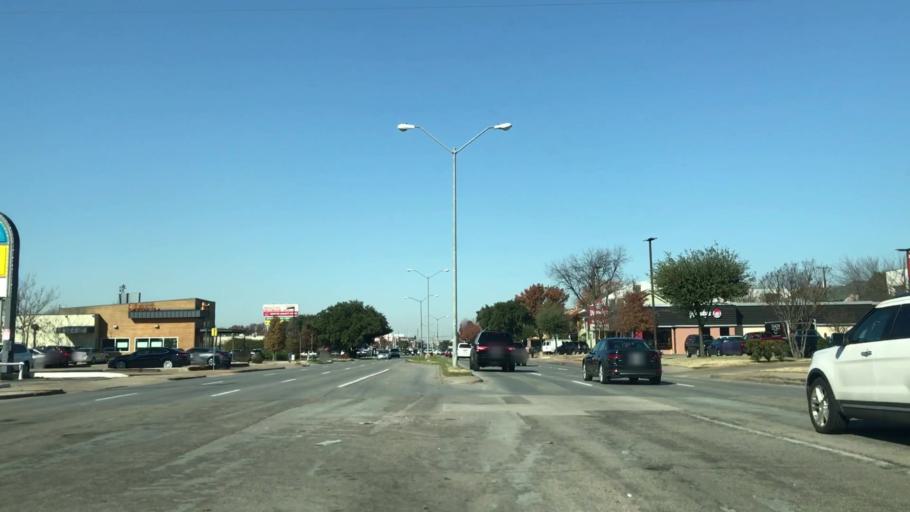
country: US
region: Texas
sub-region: Dallas County
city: Highland Park
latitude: 32.8137
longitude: -96.8077
